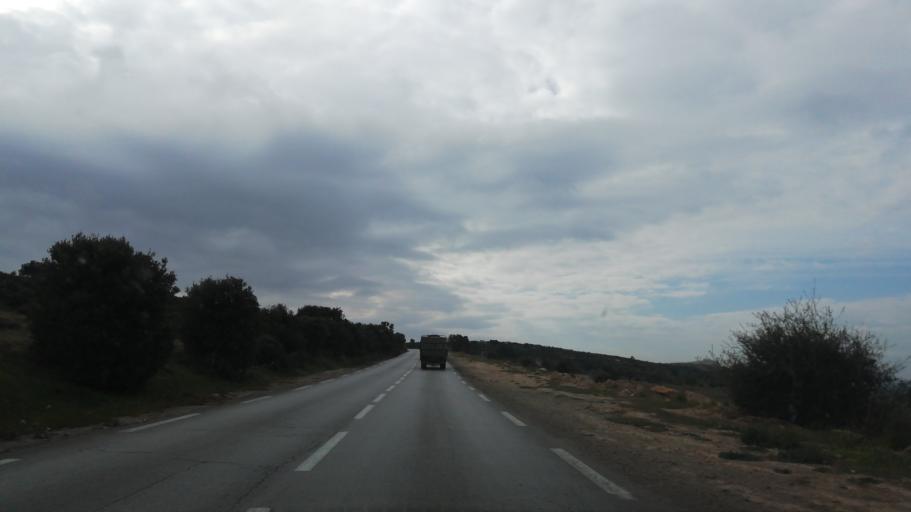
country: DZ
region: Oran
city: Ain el Bya
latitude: 35.7222
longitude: -0.3569
